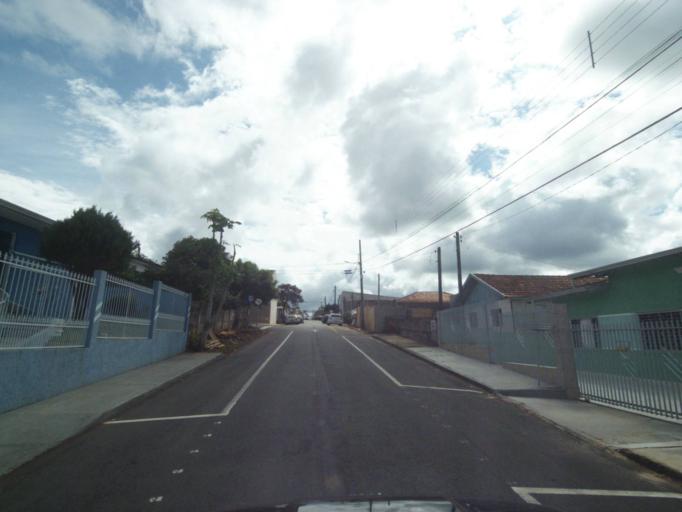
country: BR
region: Parana
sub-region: Telemaco Borba
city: Telemaco Borba
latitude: -24.3218
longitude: -50.6288
